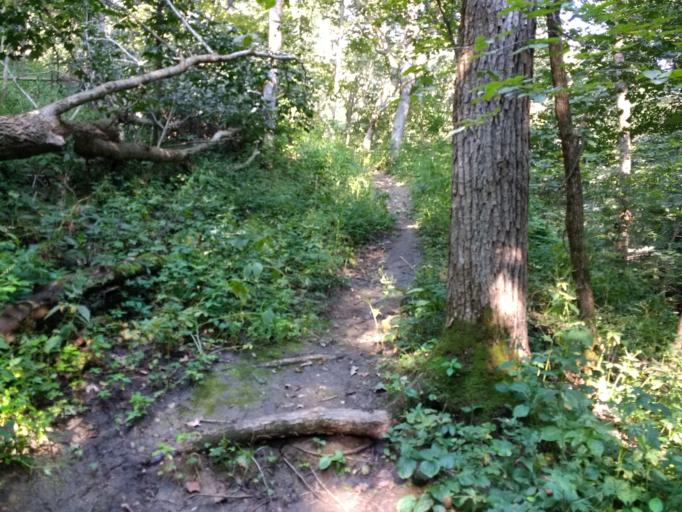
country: US
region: Iowa
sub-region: Webster County
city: Fort Dodge
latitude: 42.3994
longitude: -94.0792
